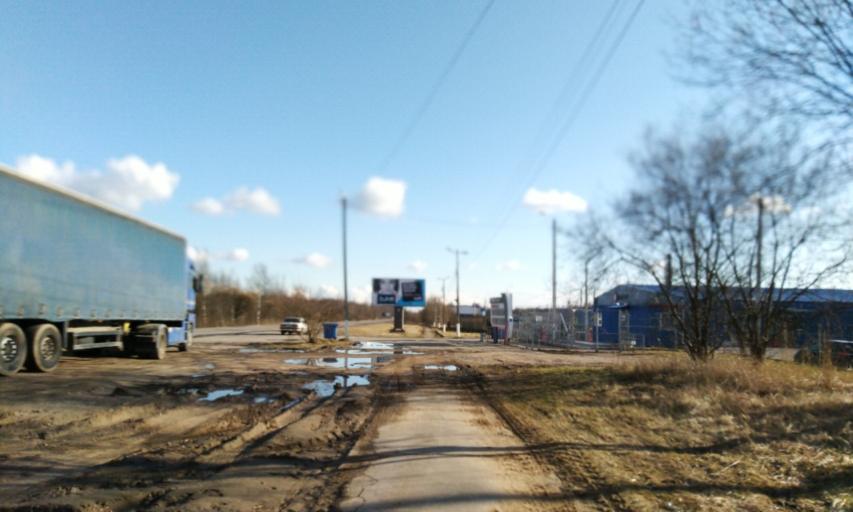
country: RU
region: Leningrad
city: Novoye Devyatkino
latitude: 60.1050
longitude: 30.4994
